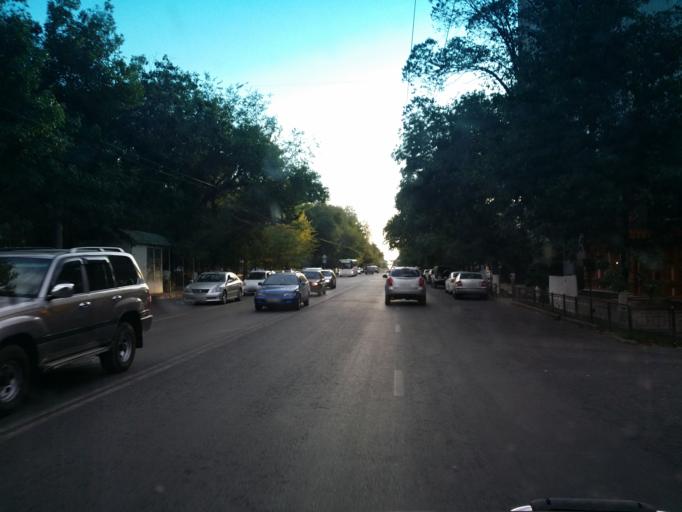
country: KZ
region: Almaty Qalasy
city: Almaty
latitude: 43.2608
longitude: 76.9578
